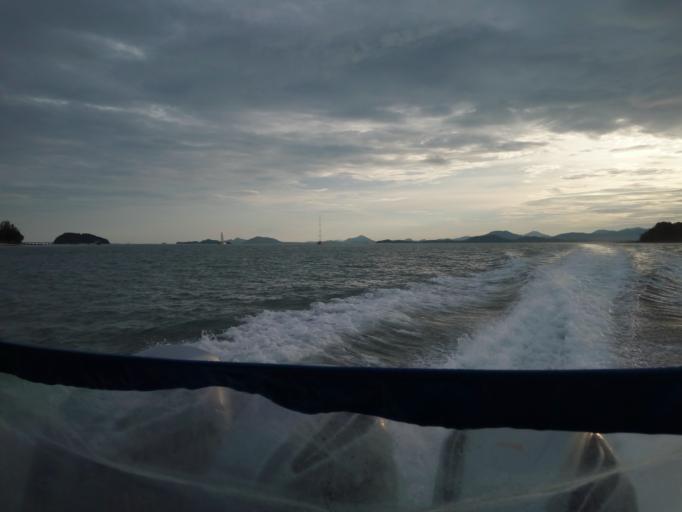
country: TH
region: Phuket
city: Thalang
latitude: 8.0624
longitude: 98.4561
